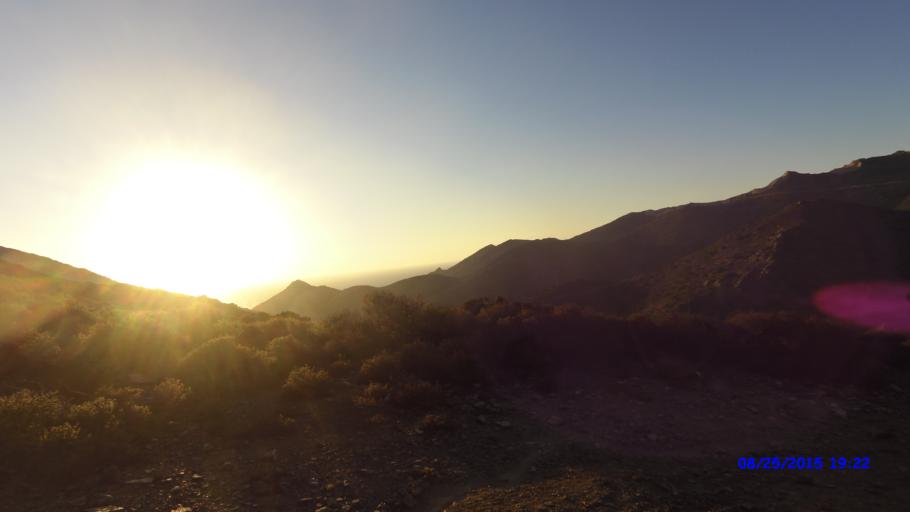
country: GR
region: South Aegean
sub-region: Nomos Kykladon
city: Antiparos
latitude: 37.0002
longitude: 25.0372
